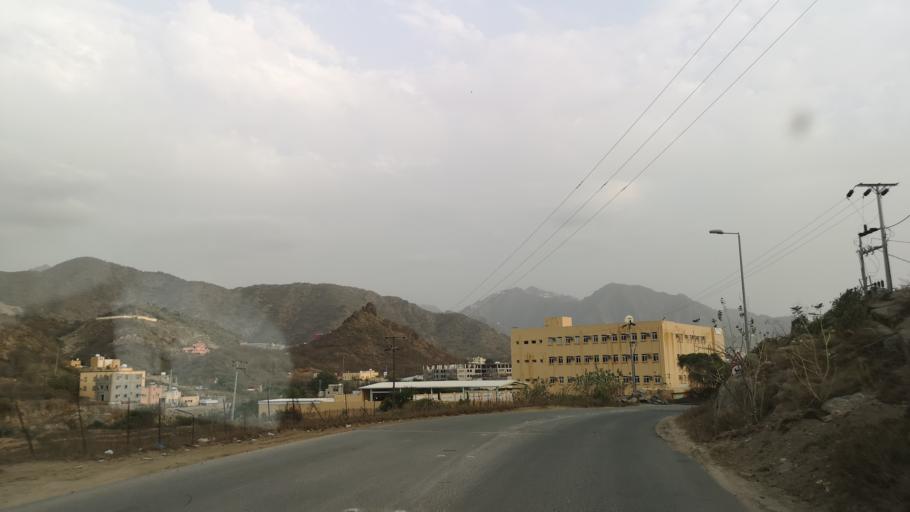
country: YE
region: Sa'dah
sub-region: Monabbih
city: Suq al Khamis
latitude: 17.3654
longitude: 43.1275
